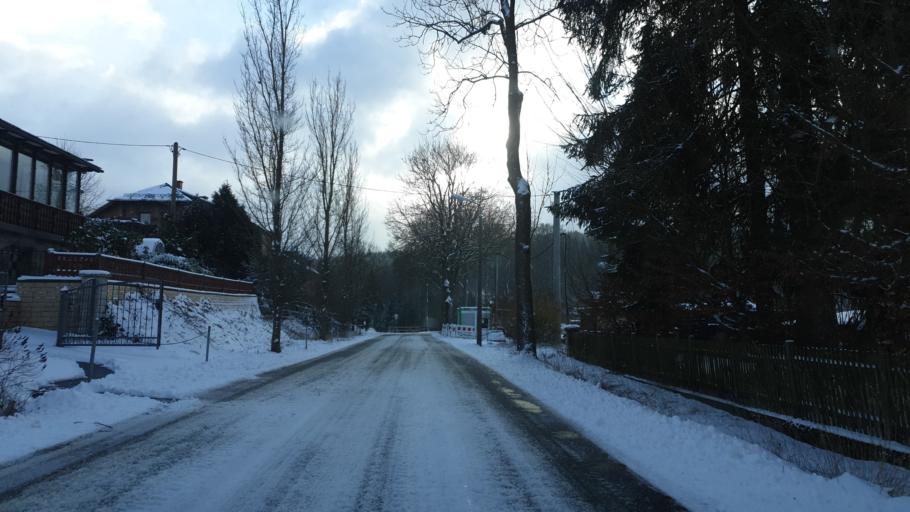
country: DE
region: Saxony
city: Bad Elster
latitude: 50.2750
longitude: 12.2477
